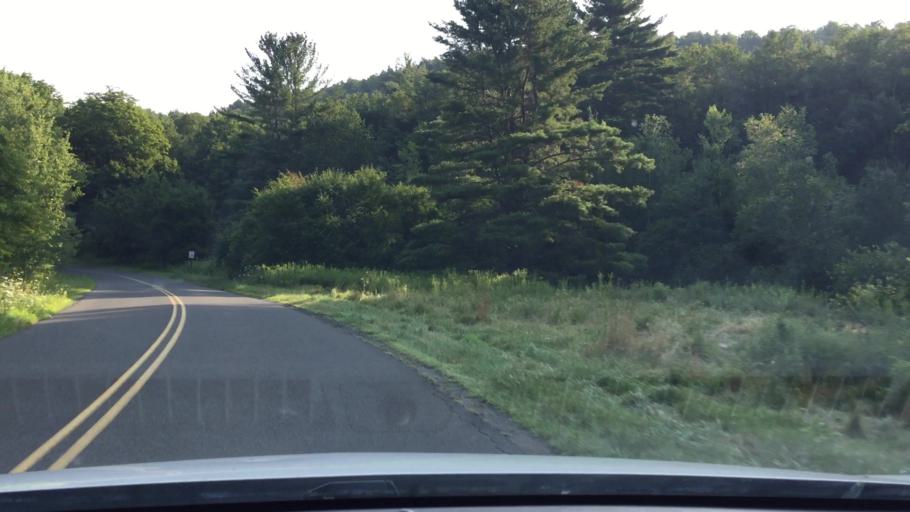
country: US
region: Massachusetts
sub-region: Berkshire County
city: Otis
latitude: 42.2366
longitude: -73.1123
